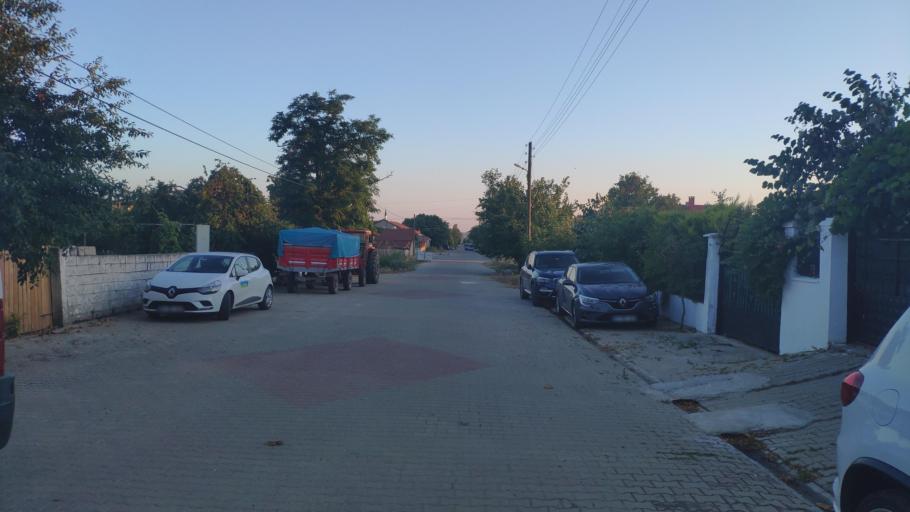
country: TR
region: Tekirdag
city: Corlu
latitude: 41.0960
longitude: 27.8187
